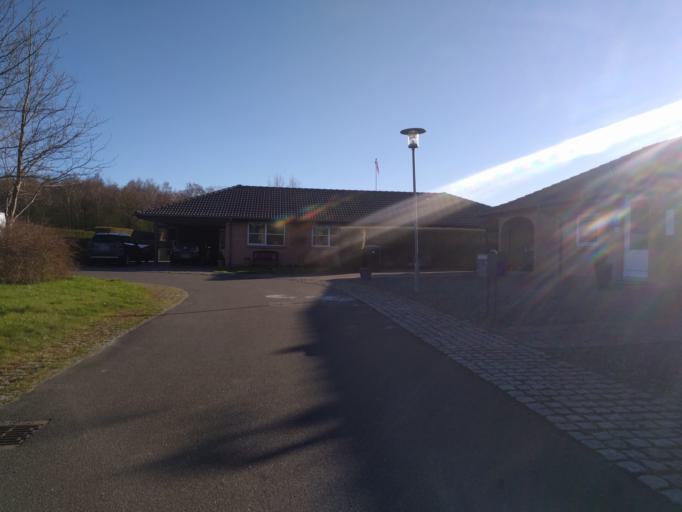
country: DK
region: South Denmark
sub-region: Odense Kommune
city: Bullerup
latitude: 55.3877
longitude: 10.5208
